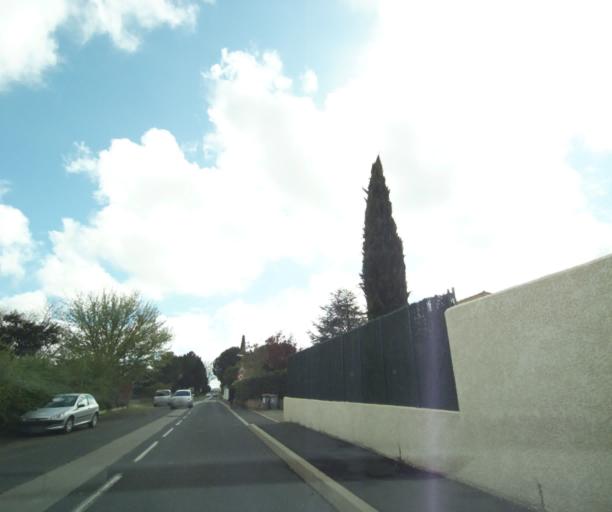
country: FR
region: Languedoc-Roussillon
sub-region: Departement de l'Herault
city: Pignan
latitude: 43.5820
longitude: 3.7570
